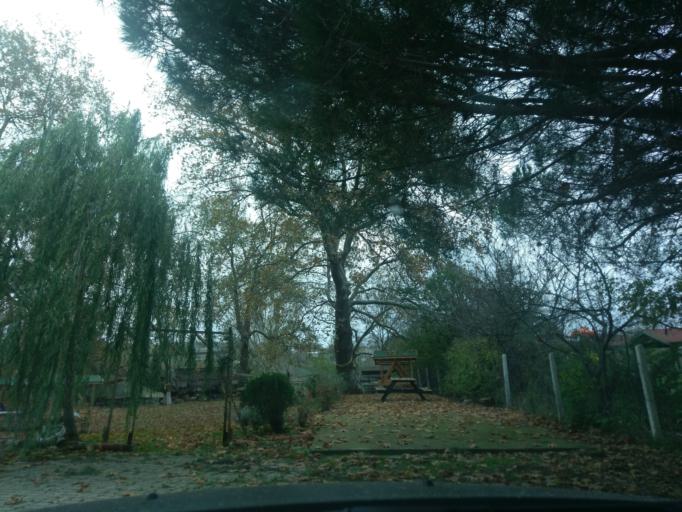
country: TR
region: Istanbul
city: Catalca
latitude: 41.1644
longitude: 28.4345
